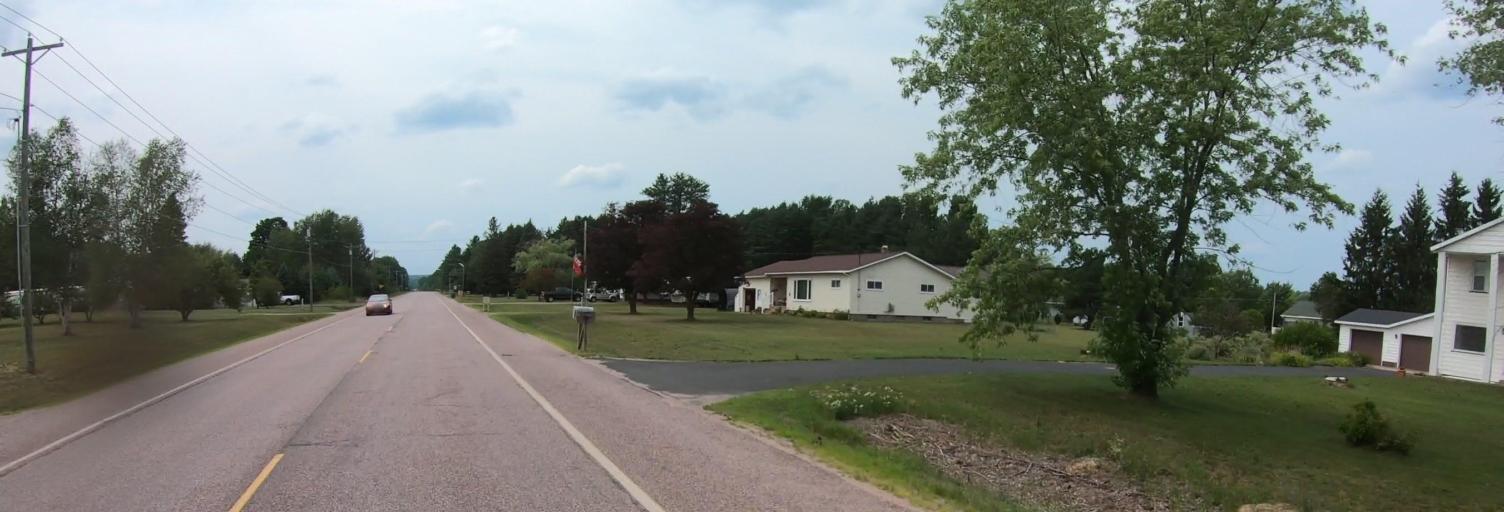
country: US
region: Michigan
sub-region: Marquette County
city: Harvey
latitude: 46.4632
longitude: -87.3388
